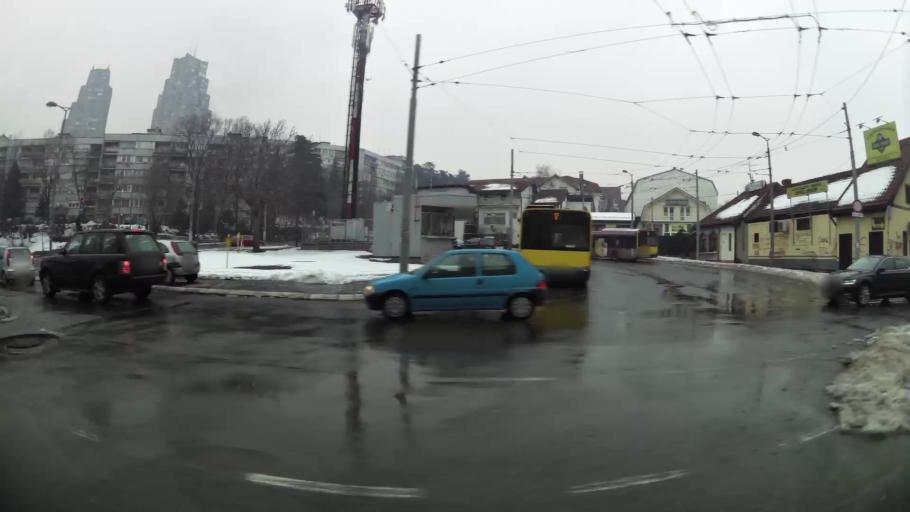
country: RS
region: Central Serbia
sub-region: Belgrade
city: Zvezdara
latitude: 44.7818
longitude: 20.5125
